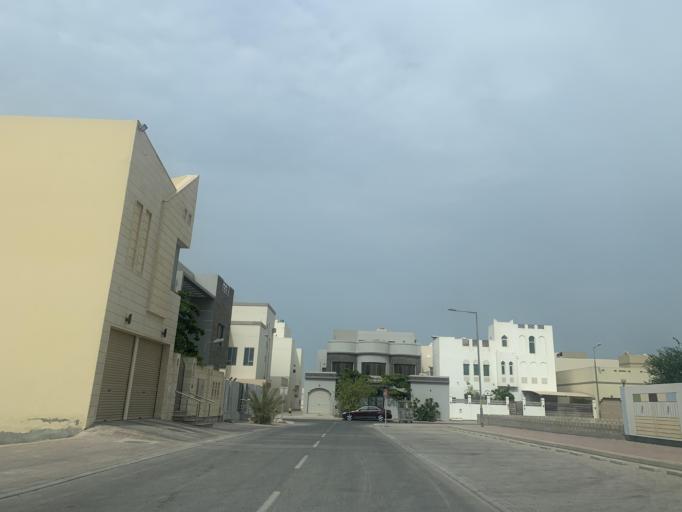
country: BH
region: Muharraq
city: Al Muharraq
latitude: 26.2854
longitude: 50.6355
